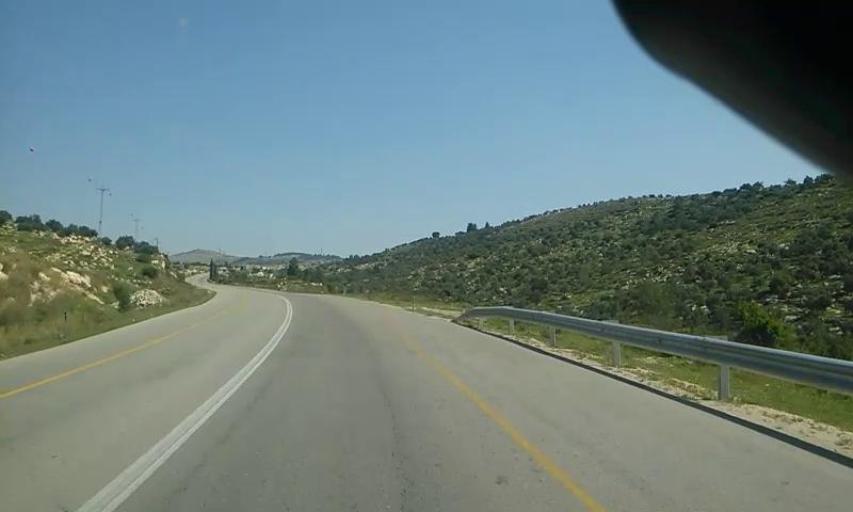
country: PS
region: West Bank
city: Tarqumya
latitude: 31.5638
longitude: 34.9972
